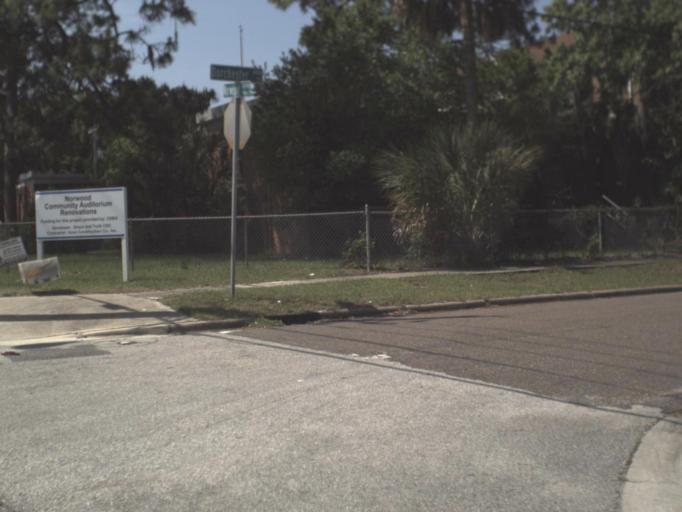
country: US
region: Florida
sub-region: Duval County
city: Jacksonville
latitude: 30.3796
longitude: -81.6700
